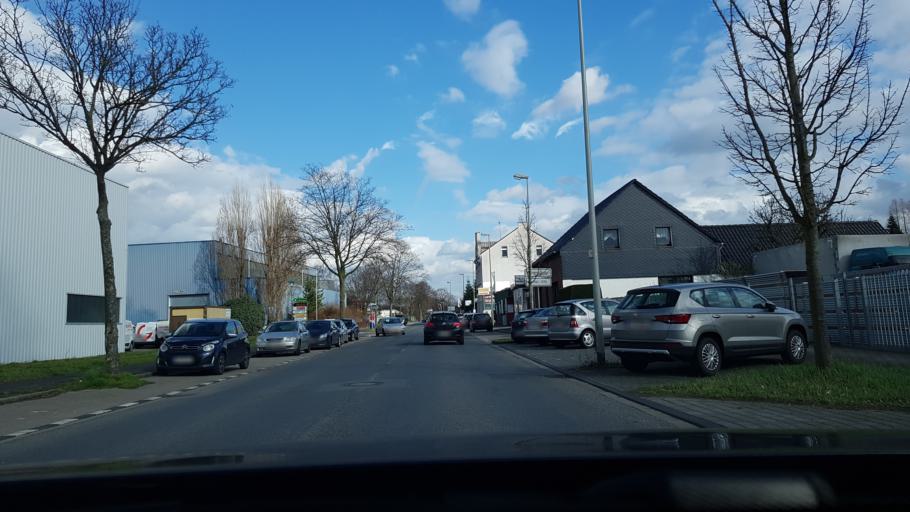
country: DE
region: North Rhine-Westphalia
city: Meiderich
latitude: 51.4906
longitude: 6.8108
